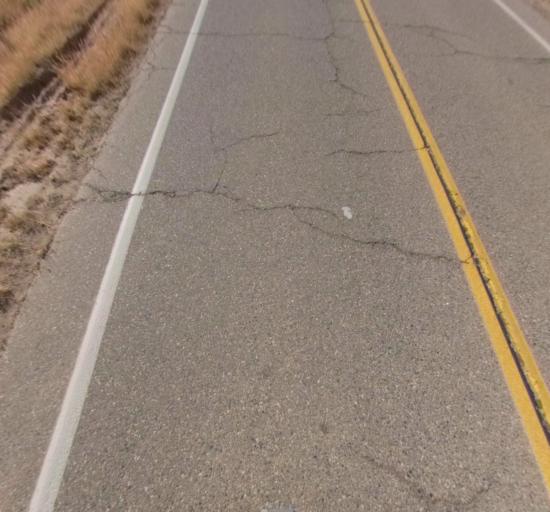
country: US
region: California
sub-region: Madera County
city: Madera Acres
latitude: 37.0098
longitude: -120.1181
